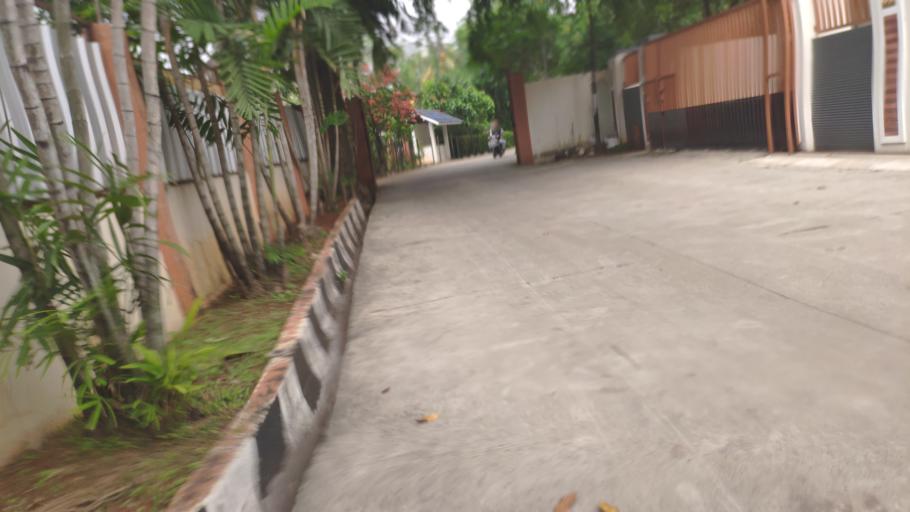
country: ID
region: Jakarta Raya
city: Jakarta
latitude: -6.2661
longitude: 106.8285
